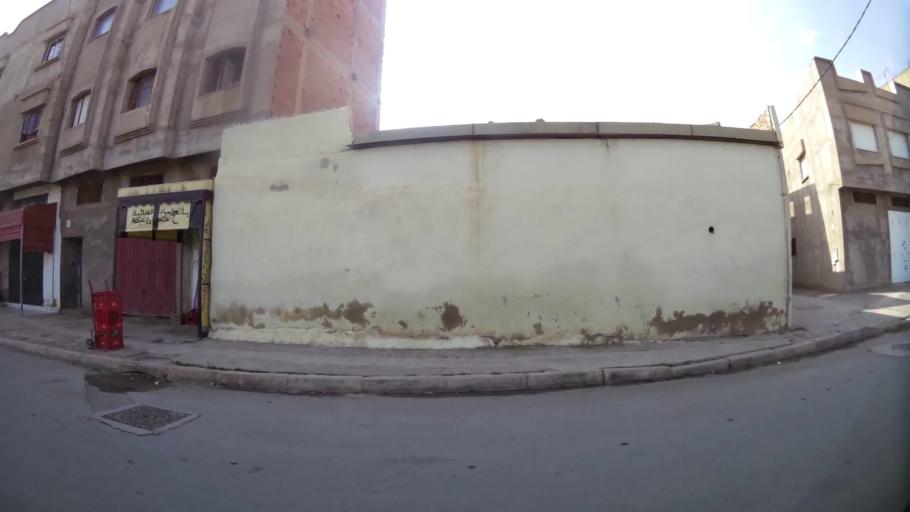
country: MA
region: Oriental
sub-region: Oujda-Angad
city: Oujda
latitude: 34.6870
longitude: -1.9013
